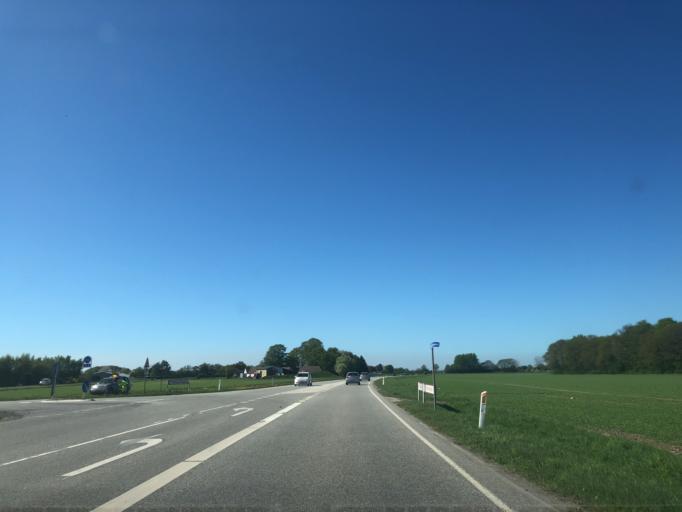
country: DK
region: Zealand
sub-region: Stevns Kommune
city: Store Heddinge
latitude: 55.3402
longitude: 12.3429
